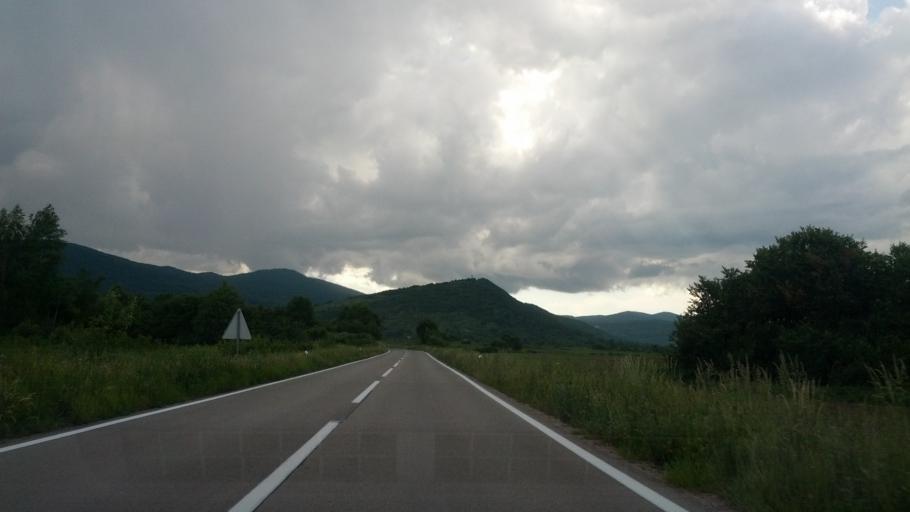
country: BA
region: Federation of Bosnia and Herzegovina
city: Izacic
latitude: 44.8780
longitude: 15.7517
